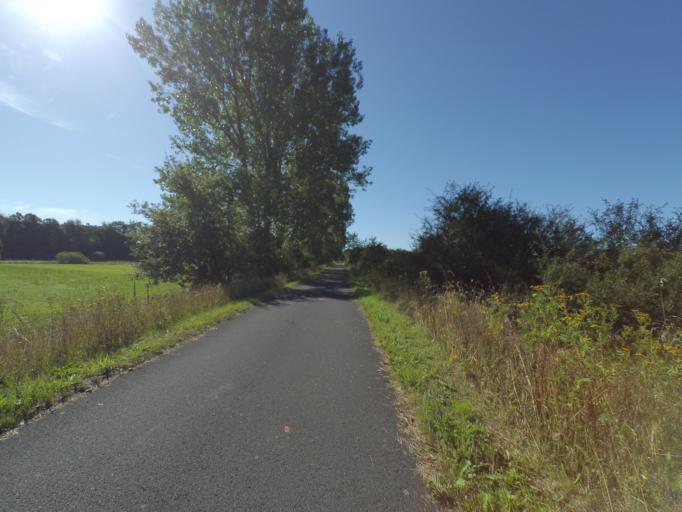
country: DE
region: Rheinland-Pfalz
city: Udler
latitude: 50.1511
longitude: 6.8774
